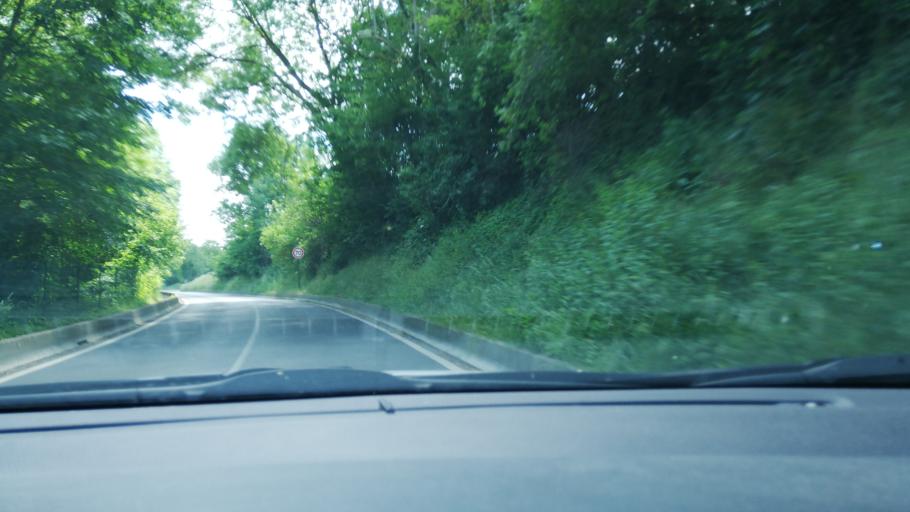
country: FR
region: Ile-de-France
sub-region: Departement du Val-d'Oise
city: Osny
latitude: 49.0713
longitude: 2.0263
